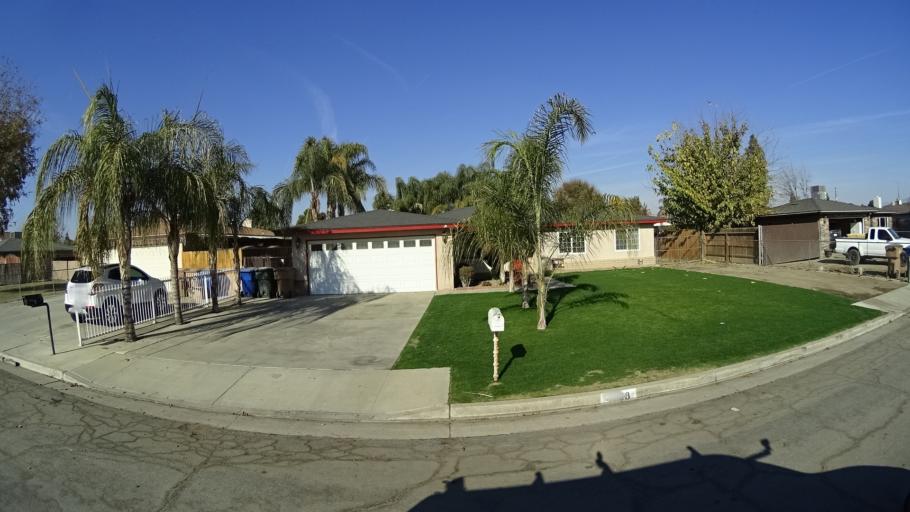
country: US
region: California
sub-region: Kern County
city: Greenfield
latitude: 35.3061
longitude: -119.0495
